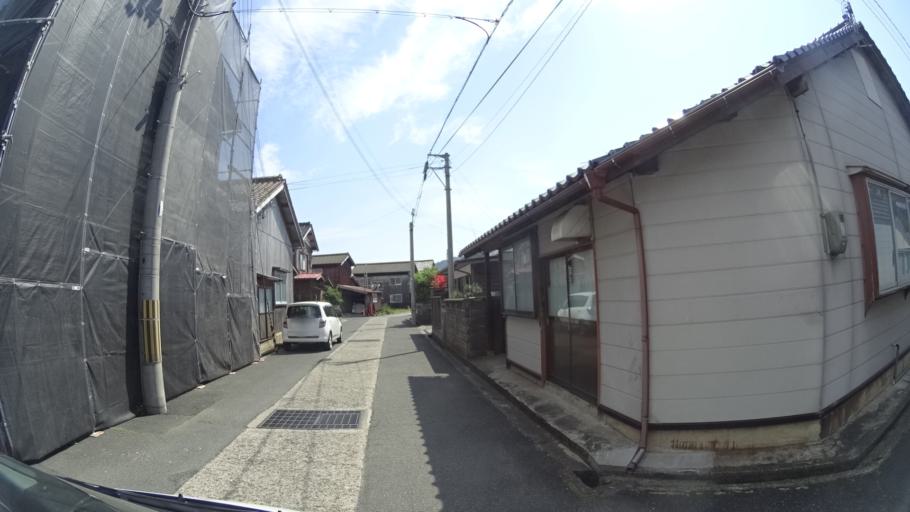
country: JP
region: Kyoto
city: Miyazu
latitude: 35.6877
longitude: 135.0290
